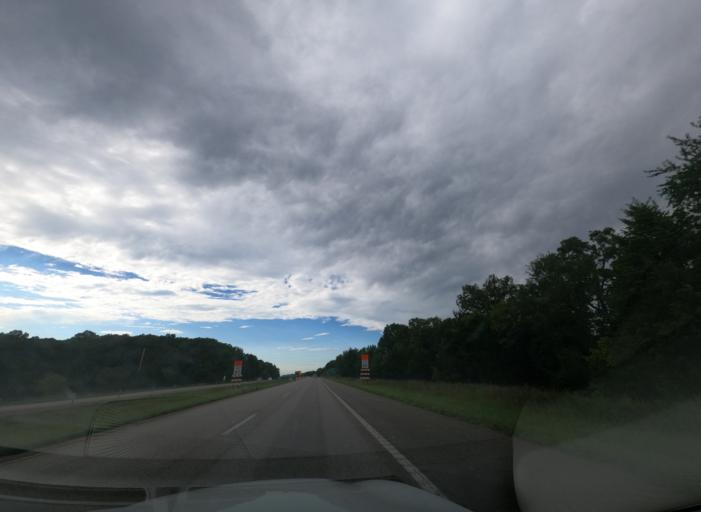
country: US
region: Missouri
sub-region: Sainte Genevieve County
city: Sainte Genevieve
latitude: 37.9850
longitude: -90.1981
